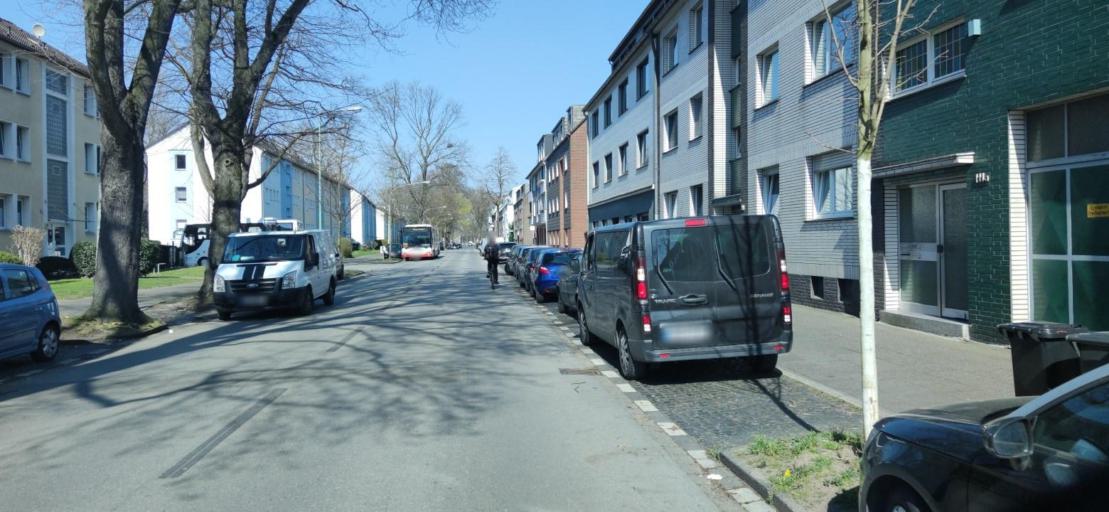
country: DE
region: North Rhine-Westphalia
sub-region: Regierungsbezirk Dusseldorf
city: Hochfeld
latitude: 51.4016
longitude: 6.7678
